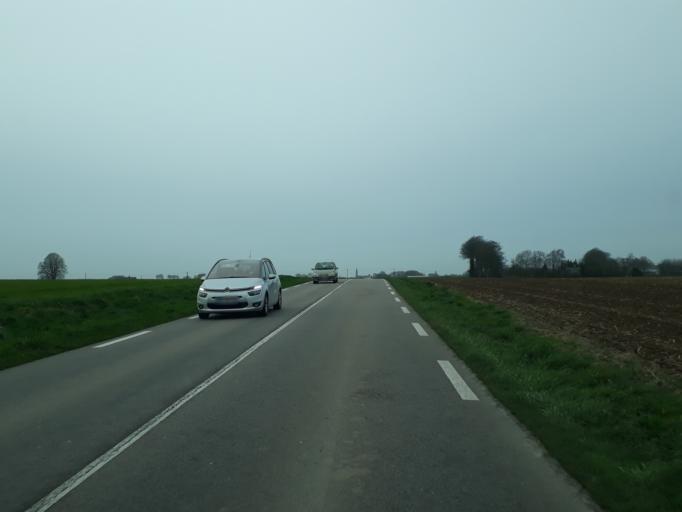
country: FR
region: Haute-Normandie
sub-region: Departement de la Seine-Maritime
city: Breaute
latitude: 49.6346
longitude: 0.3867
